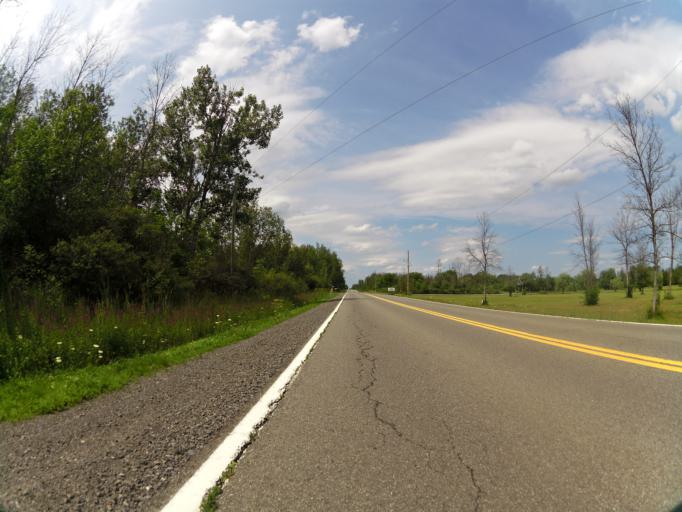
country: CA
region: Ontario
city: Ottawa
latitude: 45.2175
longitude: -75.6013
